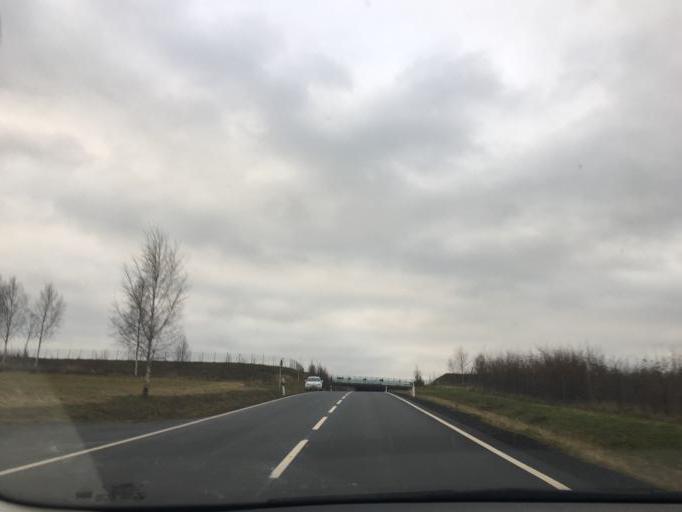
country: DE
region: Saxony
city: Hohenstein-Ernstthal
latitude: 50.8111
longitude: 12.7044
